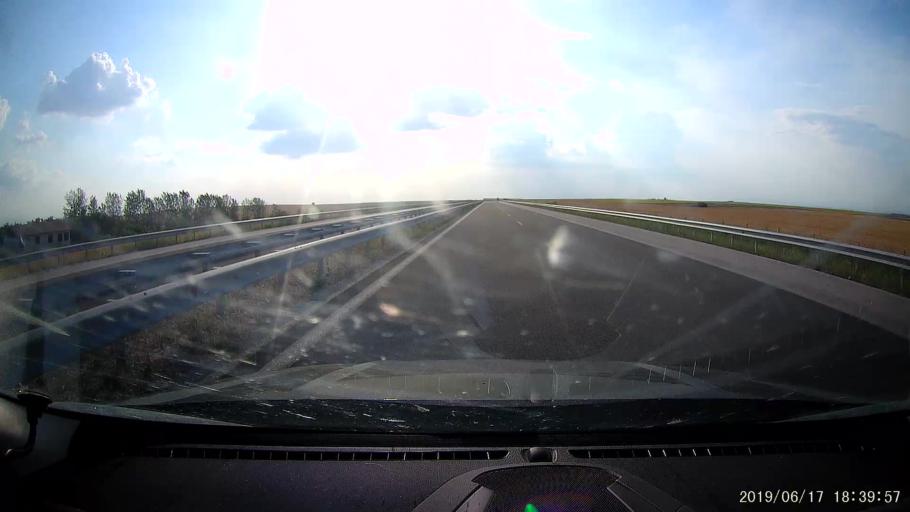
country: BG
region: Stara Zagora
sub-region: Obshtina Chirpan
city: Chirpan
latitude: 42.1501
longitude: 25.2919
